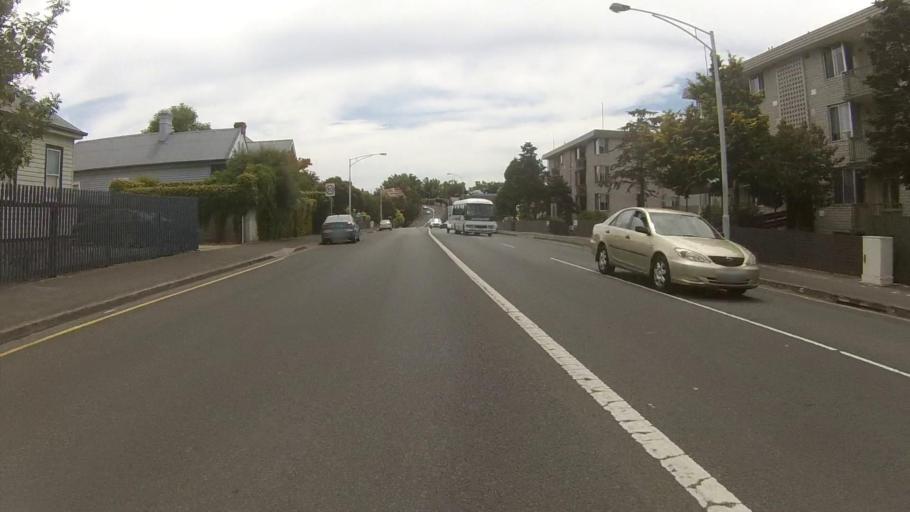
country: AU
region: Tasmania
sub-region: Hobart
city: Sandy Bay
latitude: -42.8954
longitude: 147.3232
